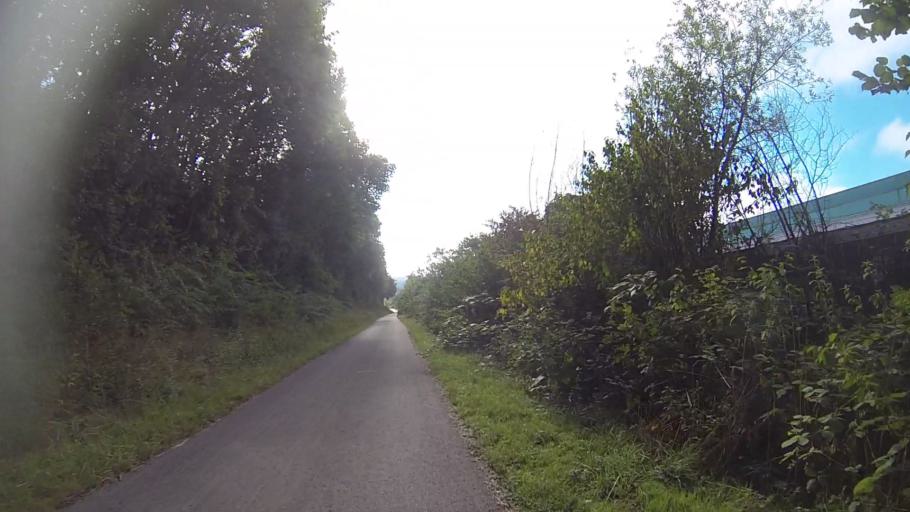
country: DE
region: Rheinland-Pfalz
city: Kenn
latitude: 49.8016
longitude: 6.6963
